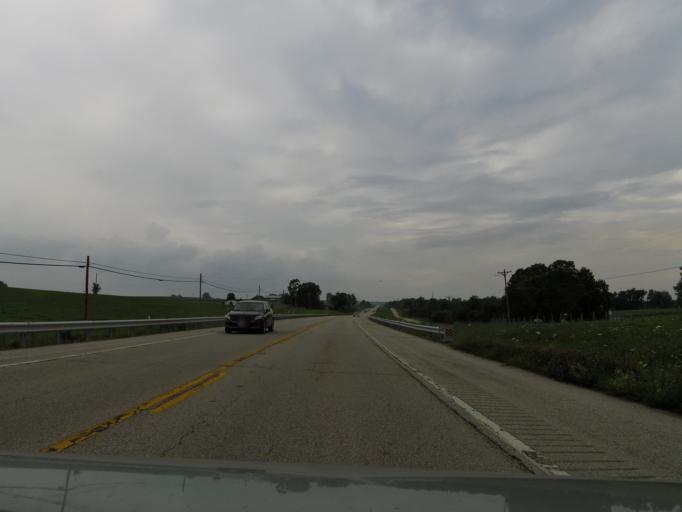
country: US
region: Kentucky
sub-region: Mason County
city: Maysville
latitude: 38.5452
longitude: -83.8240
